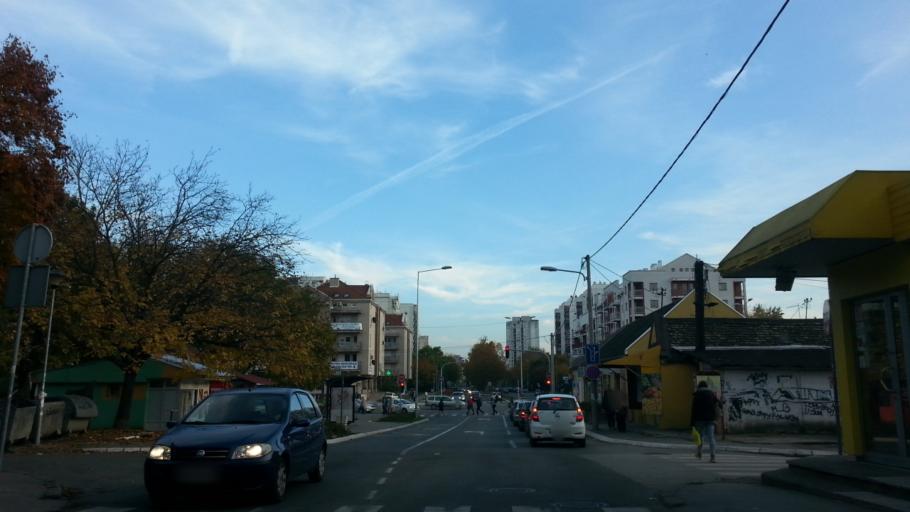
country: RS
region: Central Serbia
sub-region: Belgrade
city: Zemun
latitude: 44.8111
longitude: 20.3821
